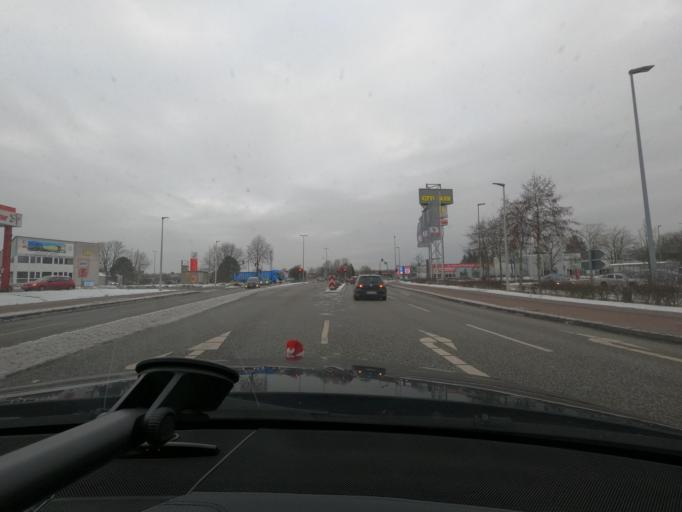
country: DE
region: Schleswig-Holstein
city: Harrislee
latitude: 54.7744
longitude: 9.3947
